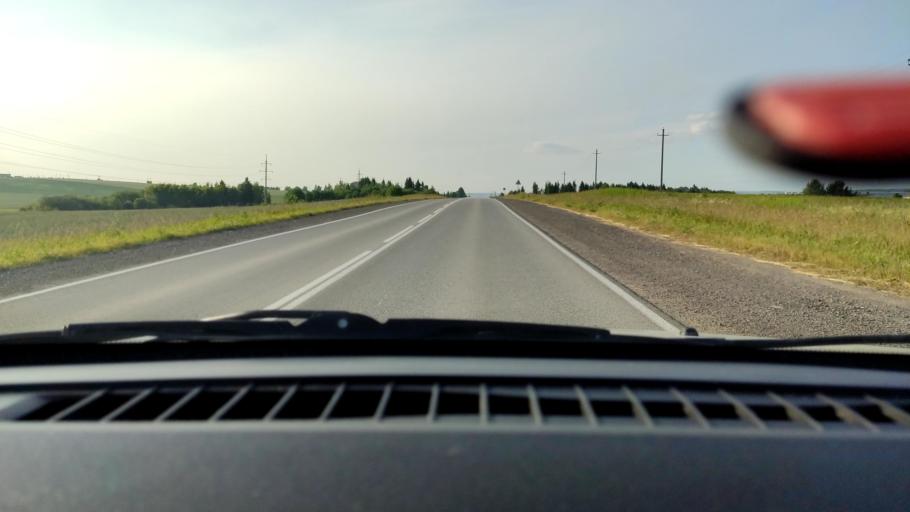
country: RU
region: Perm
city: Lobanovo
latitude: 57.8494
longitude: 56.2964
